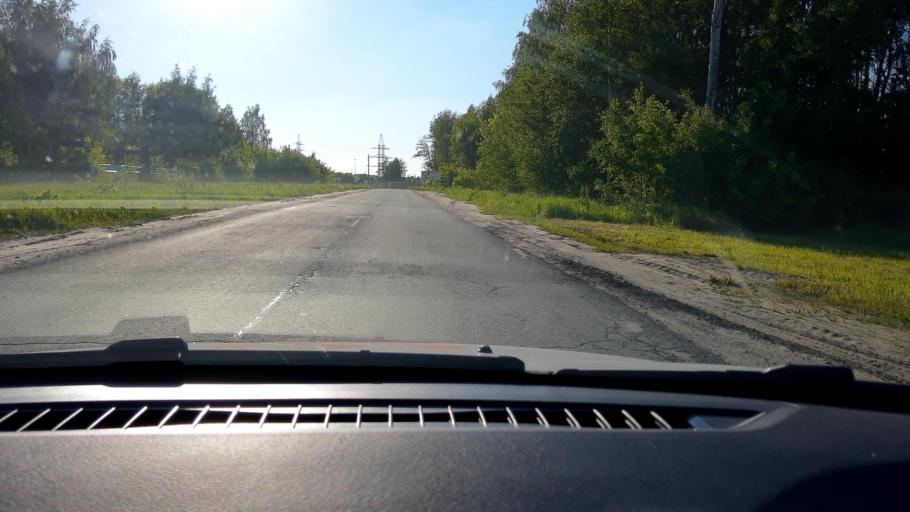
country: RU
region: Nizjnij Novgorod
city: Kstovo
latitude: 56.1039
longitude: 44.1316
